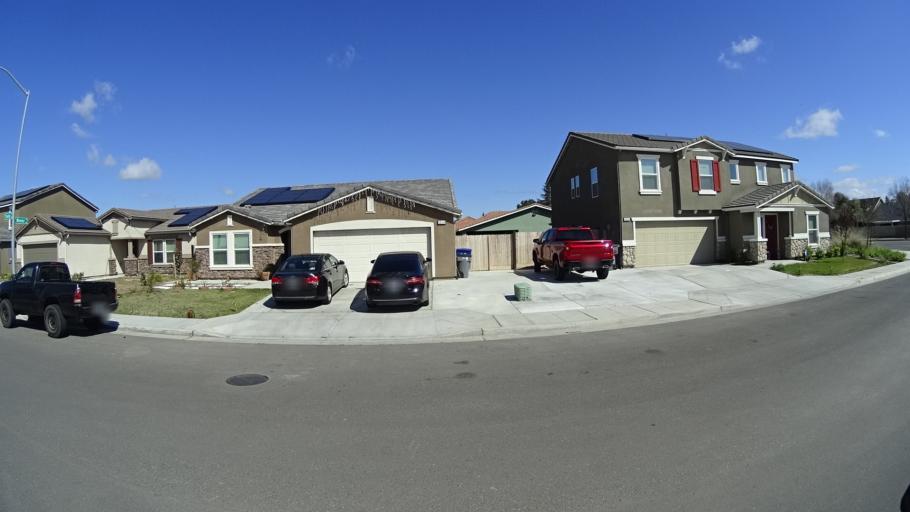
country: US
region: California
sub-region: Fresno County
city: West Park
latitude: 36.7895
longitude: -119.8899
